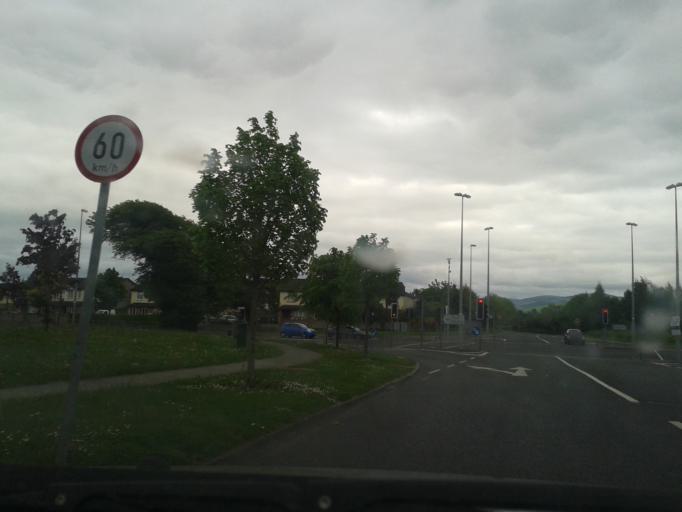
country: IE
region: Leinster
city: Clondalkin
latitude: 53.3211
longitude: -6.4224
